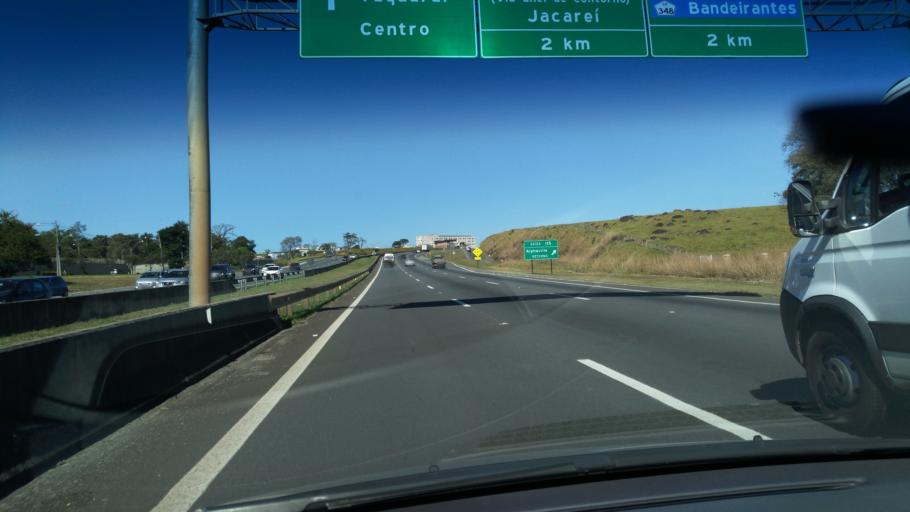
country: BR
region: Sao Paulo
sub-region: Campinas
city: Campinas
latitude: -22.8257
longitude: -47.0358
